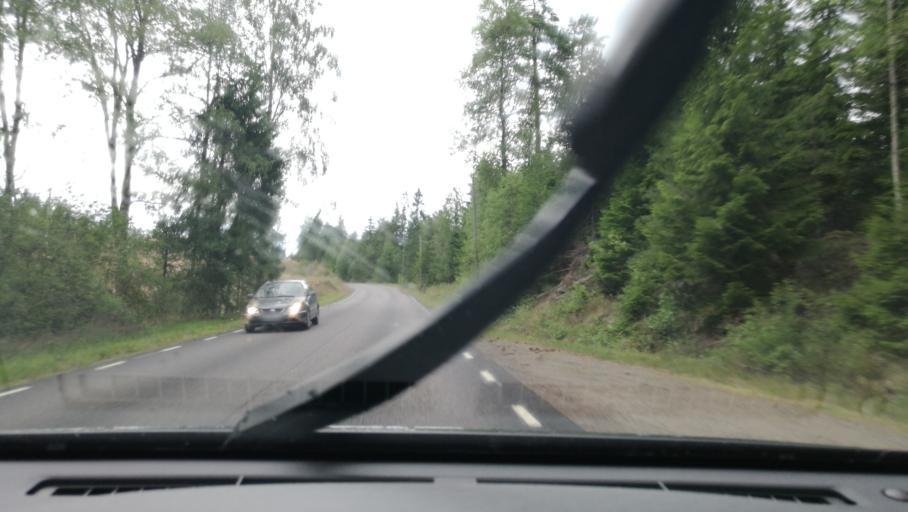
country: SE
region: OEstergoetland
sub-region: Norrkopings Kommun
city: Jursla
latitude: 58.8000
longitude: 16.1458
